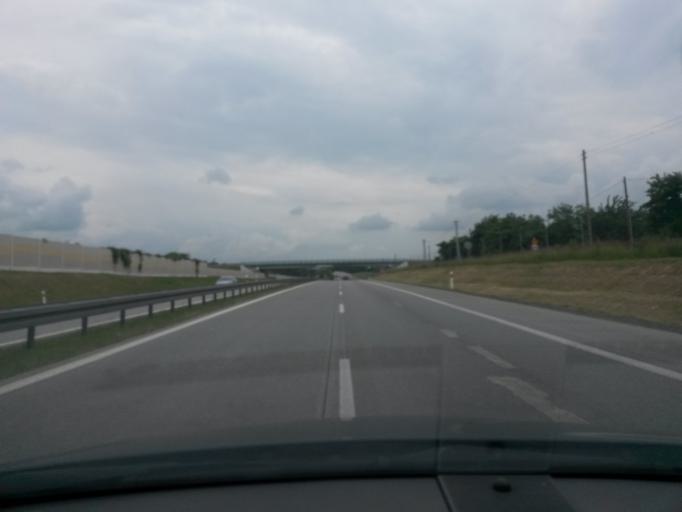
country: PL
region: Lodz Voivodeship
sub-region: Powiat skierniewicki
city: Kowiesy
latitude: 51.8804
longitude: 20.3996
